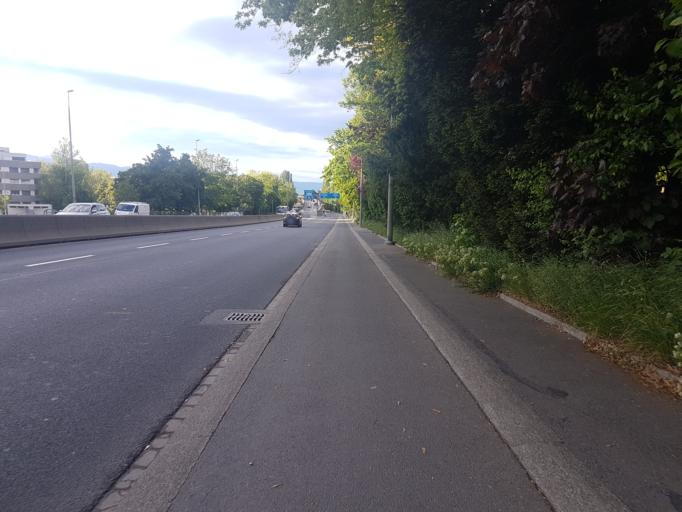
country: CH
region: Geneva
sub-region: Geneva
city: Les Avanchets
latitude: 46.2072
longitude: 6.1100
